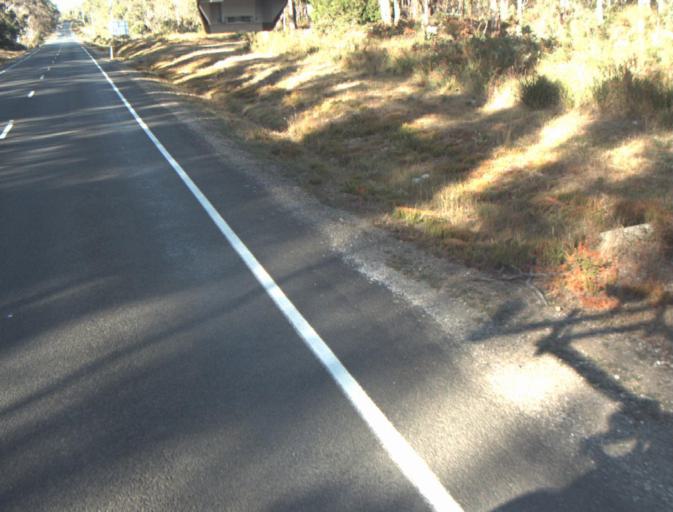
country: AU
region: Tasmania
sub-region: Launceston
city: Mayfield
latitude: -41.3135
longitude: 147.1971
